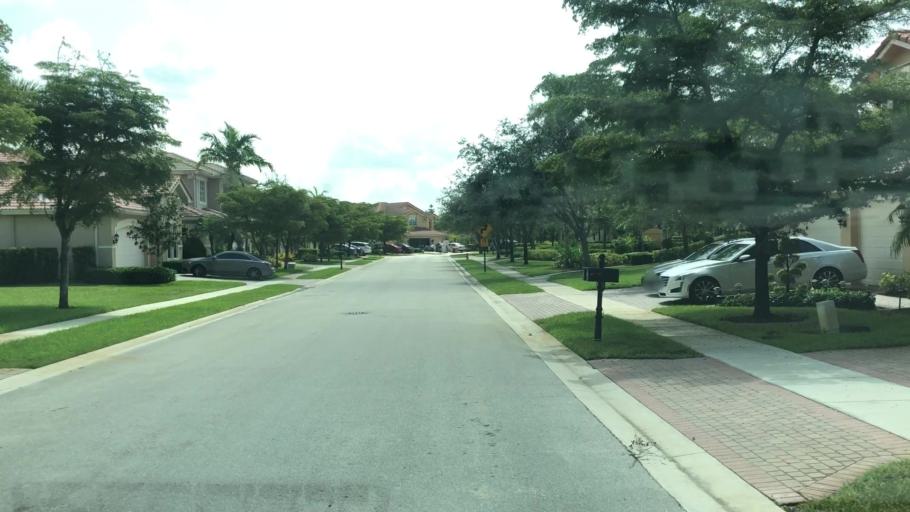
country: US
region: Florida
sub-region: Miami-Dade County
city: Palm Springs North
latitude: 25.9655
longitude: -80.3806
